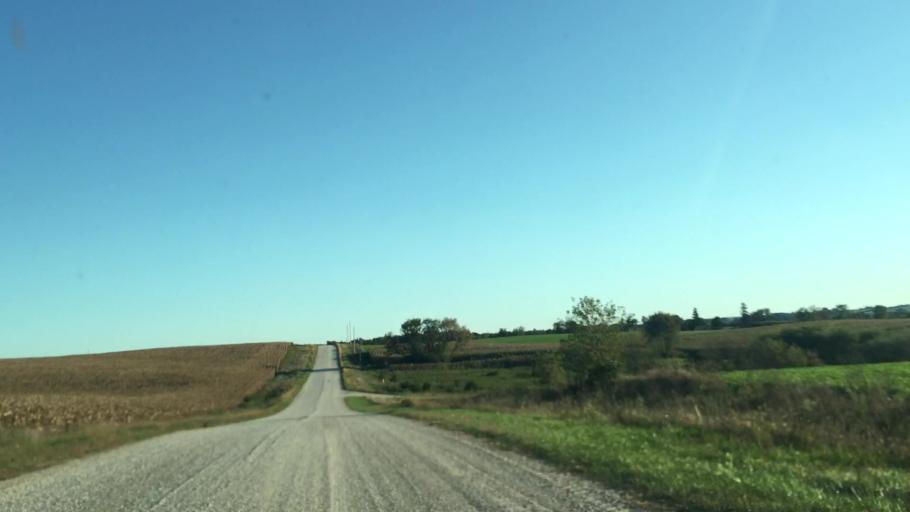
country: US
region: Minnesota
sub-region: Fillmore County
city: Preston
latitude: 43.7986
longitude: -92.0394
